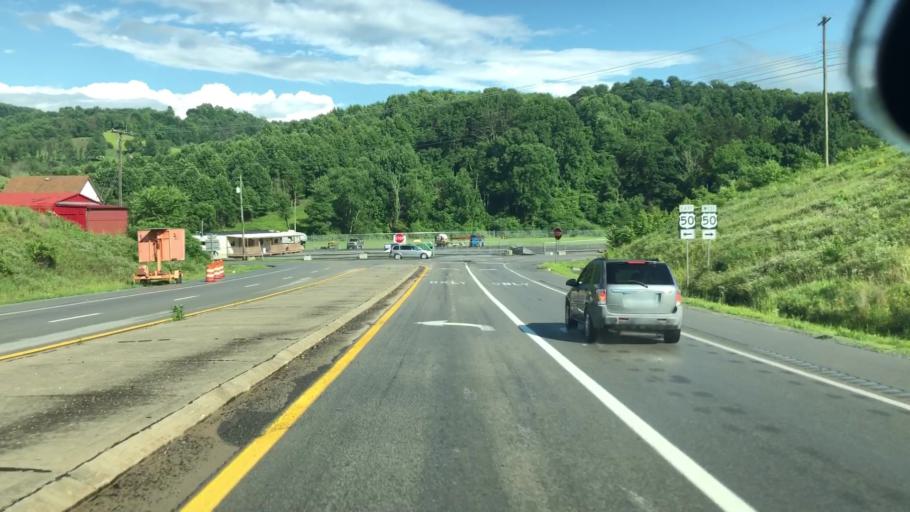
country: US
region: West Virginia
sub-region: Harrison County
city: Bridgeport
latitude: 39.2984
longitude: -80.2053
